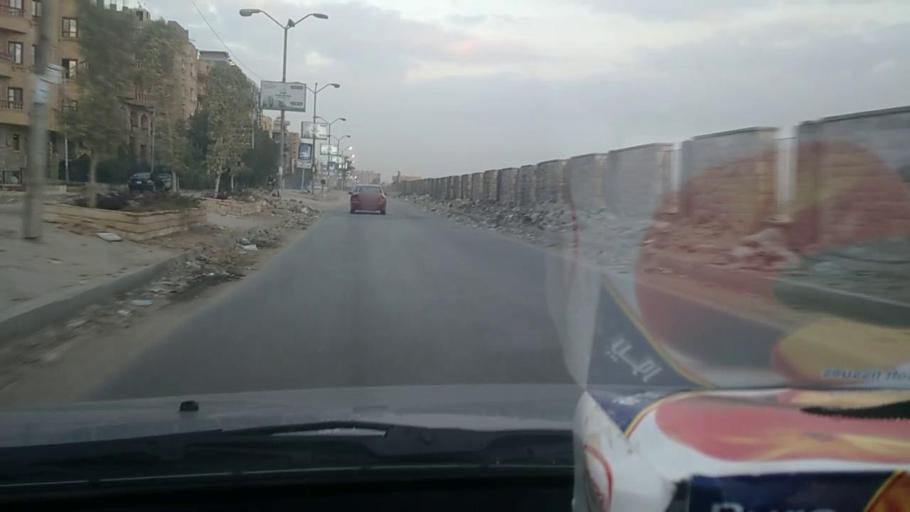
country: EG
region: Muhafazat al Qahirah
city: Cairo
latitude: 29.9967
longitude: 31.2900
